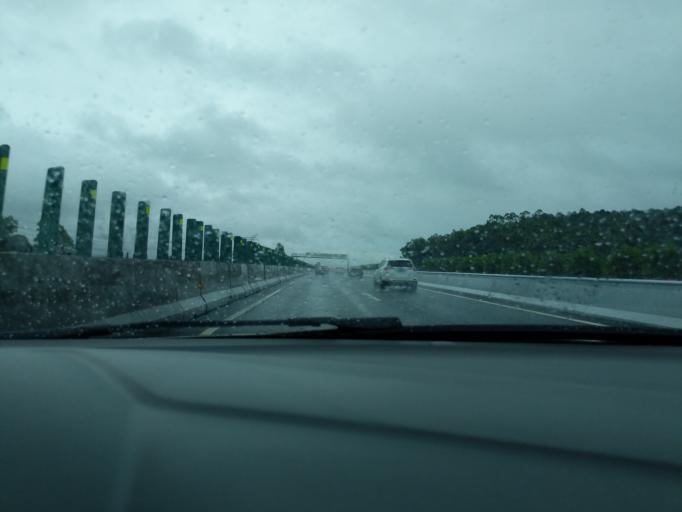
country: CN
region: Guangdong
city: Pingshi
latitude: 22.2581
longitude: 112.3126
